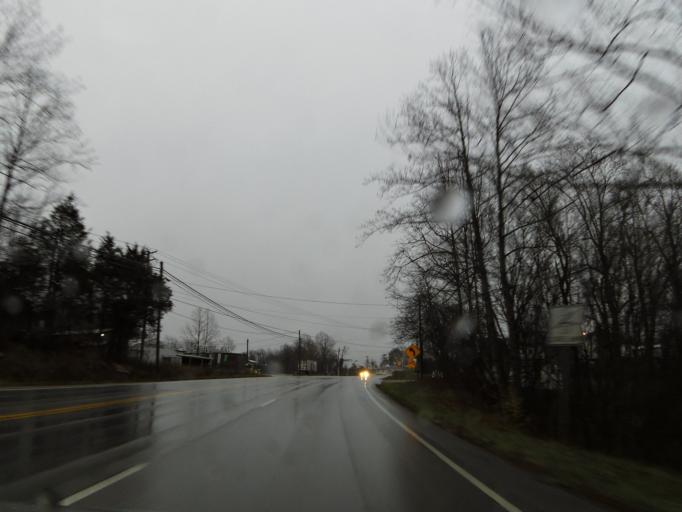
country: US
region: Kentucky
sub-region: Rockcastle County
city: Mount Vernon
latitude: 37.3482
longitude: -84.3265
